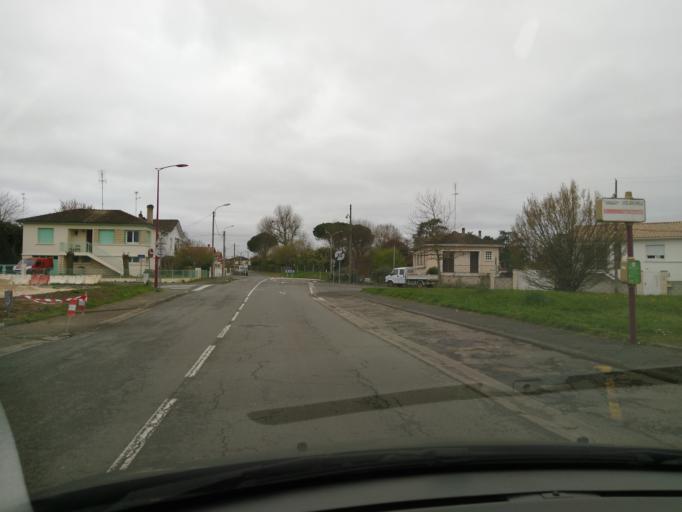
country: FR
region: Aquitaine
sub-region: Departement de la Dordogne
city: Bergerac
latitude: 44.8436
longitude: 0.4754
